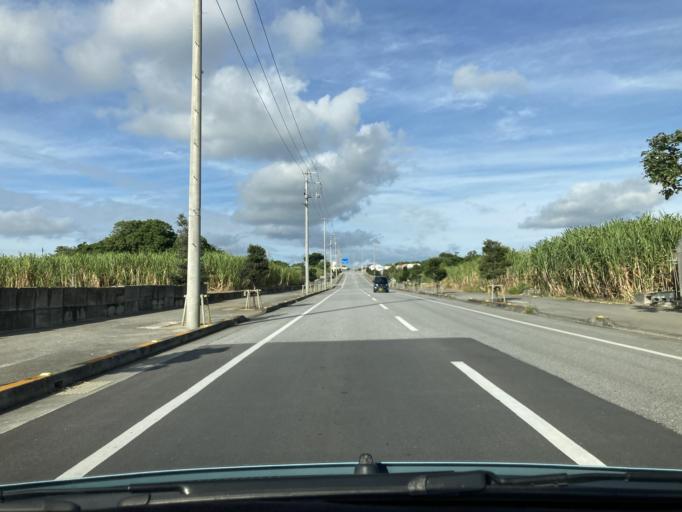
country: JP
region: Okinawa
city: Itoman
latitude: 26.1266
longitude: 127.6820
